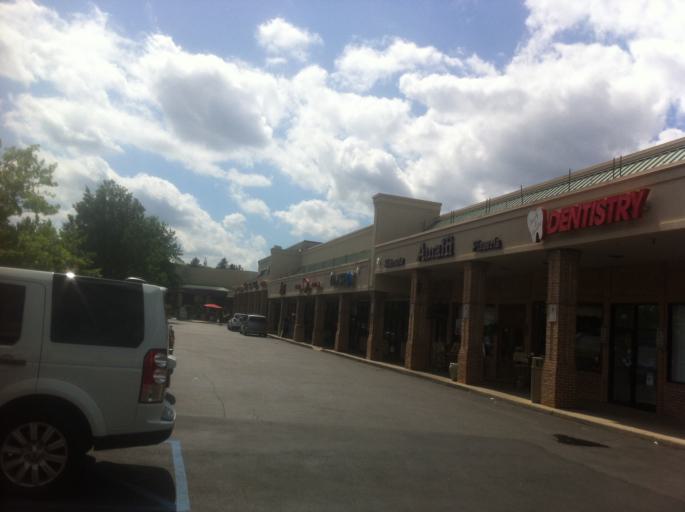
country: US
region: New York
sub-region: Nassau County
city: Glen Cove
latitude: 40.8747
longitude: -73.6193
